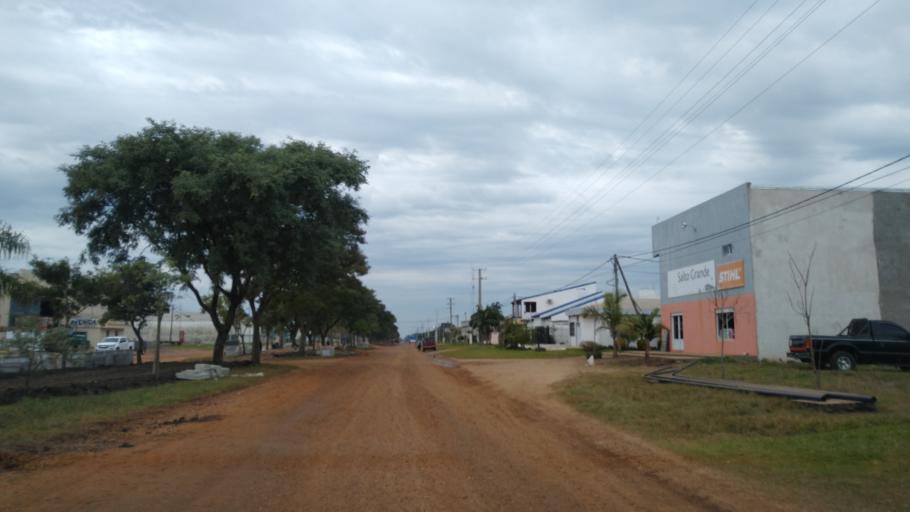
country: AR
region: Entre Rios
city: Villa del Rosario
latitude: -30.7950
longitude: -57.9183
